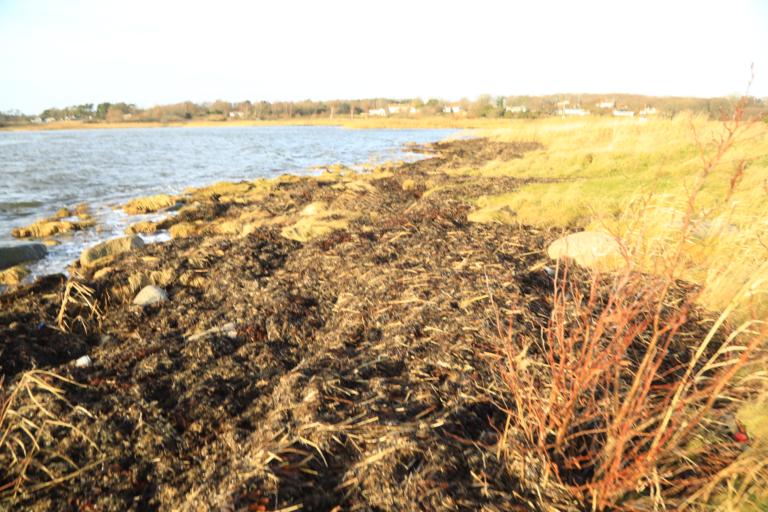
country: SE
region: Halland
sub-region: Varbergs Kommun
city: Varberg
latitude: 57.1891
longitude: 12.2047
